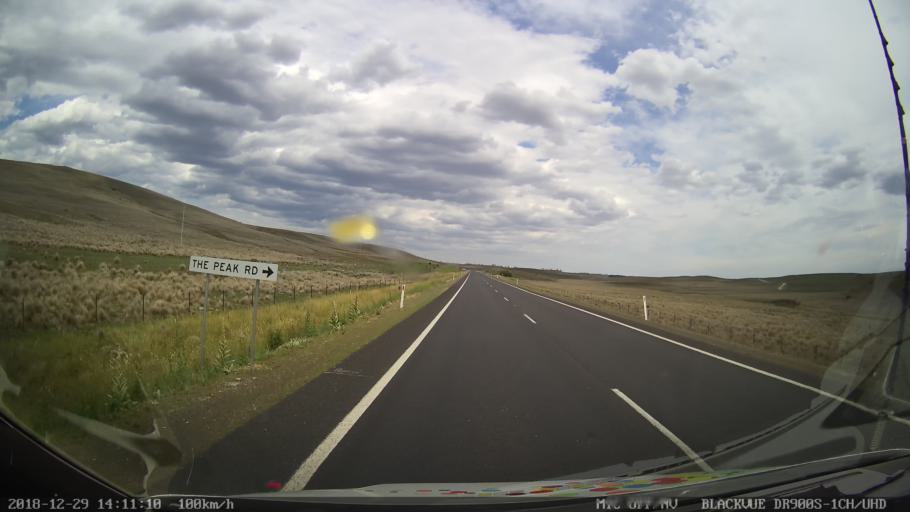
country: AU
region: New South Wales
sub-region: Cooma-Monaro
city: Cooma
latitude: -36.4021
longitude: 149.2186
